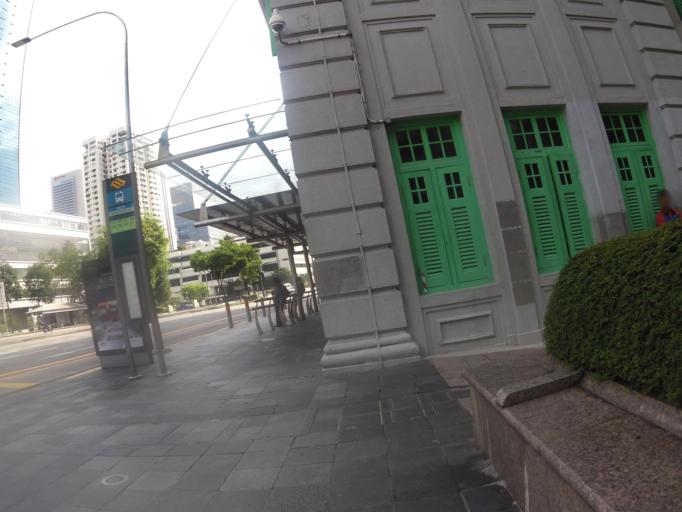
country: SG
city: Singapore
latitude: 1.2911
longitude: 103.8487
